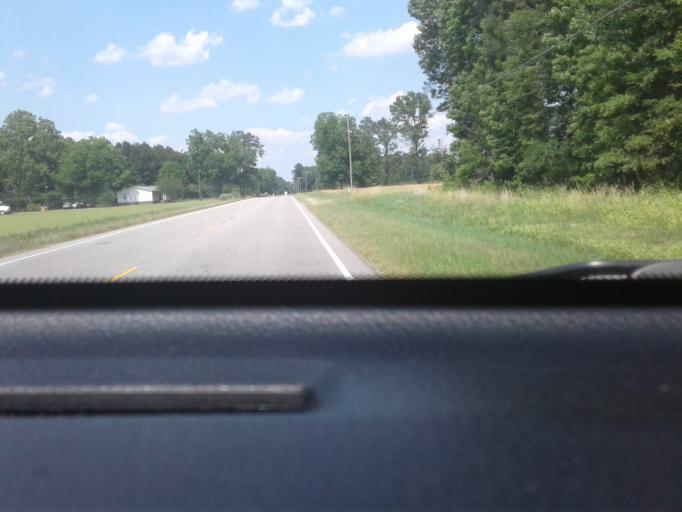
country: US
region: North Carolina
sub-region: Cumberland County
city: Eastover
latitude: 35.1283
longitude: -78.7568
